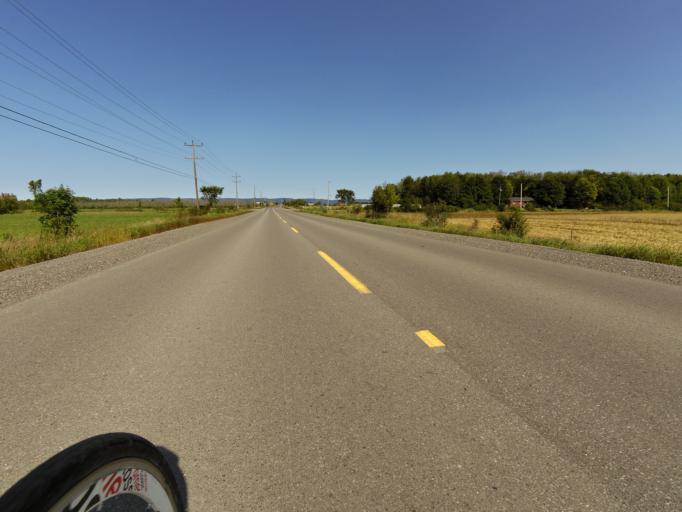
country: CA
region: Ontario
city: Arnprior
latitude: 45.4433
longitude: -76.1046
